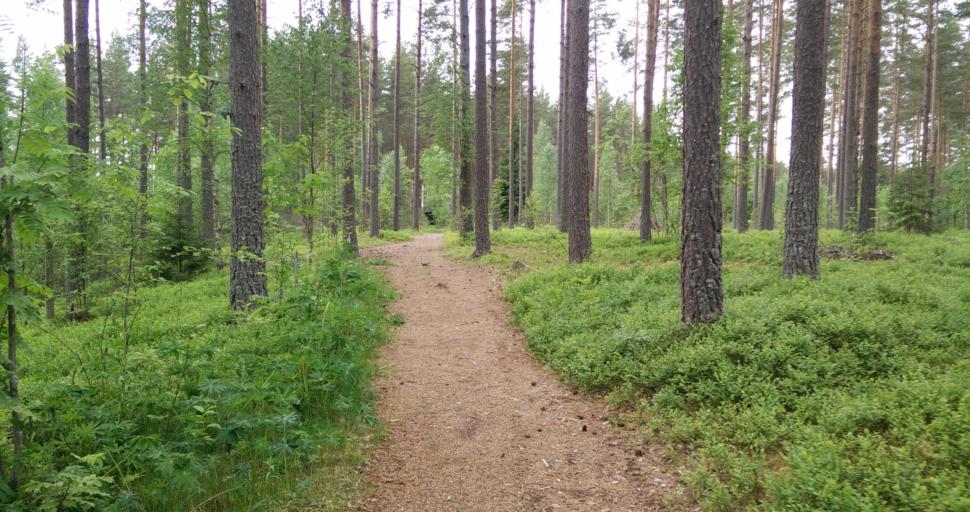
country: SE
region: Vaermland
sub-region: Hagfors Kommun
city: Hagfors
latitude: 60.0103
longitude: 13.5882
